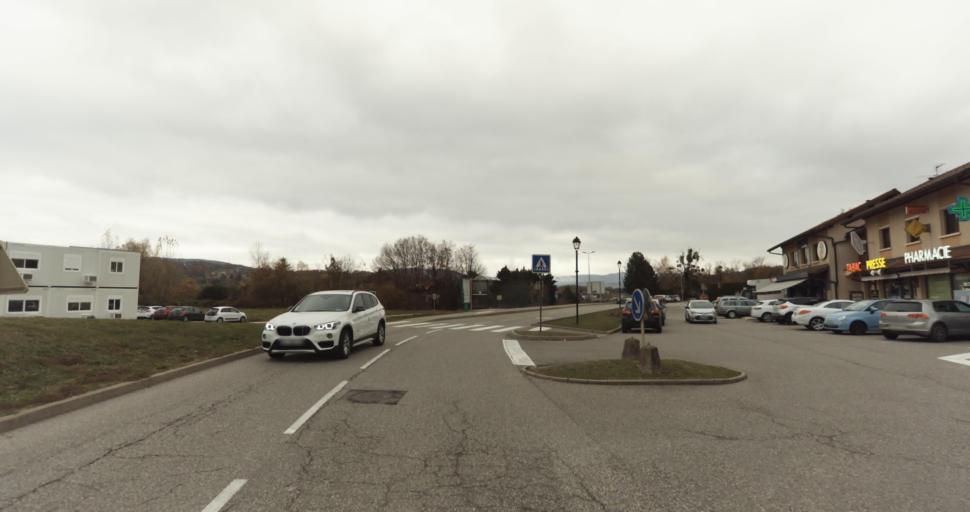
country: FR
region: Rhone-Alpes
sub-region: Departement de la Haute-Savoie
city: Pringy
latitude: 45.9640
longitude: 6.1320
